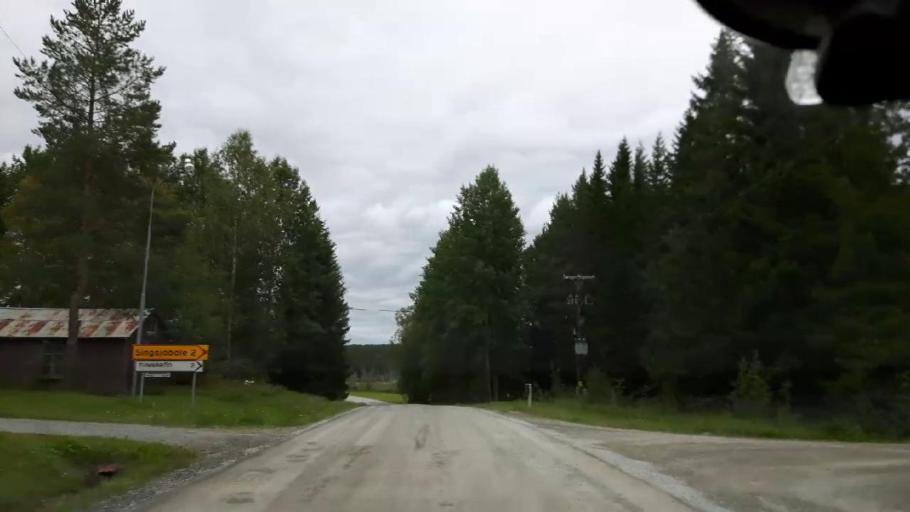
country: SE
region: Jaemtland
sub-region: OEstersunds Kommun
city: Brunflo
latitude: 63.0896
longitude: 15.1444
